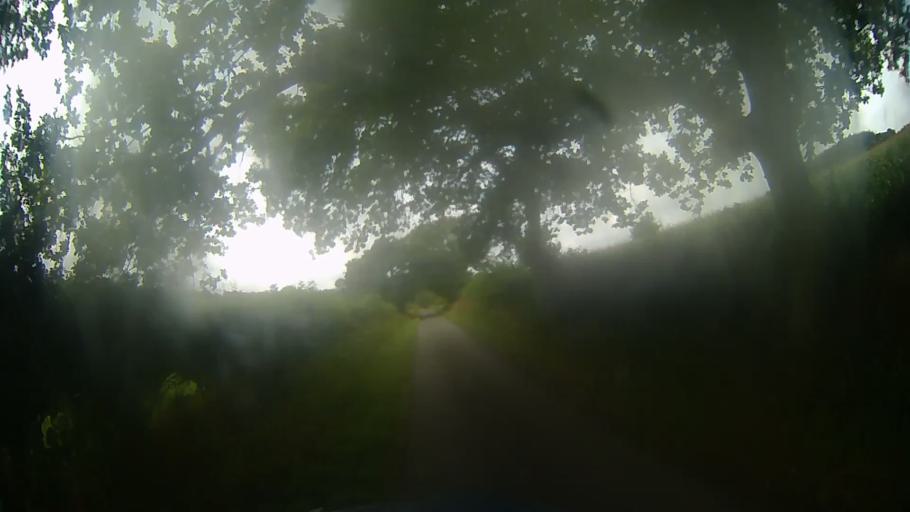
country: GB
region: England
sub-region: Hampshire
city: Overton
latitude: 51.2700
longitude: -1.3178
